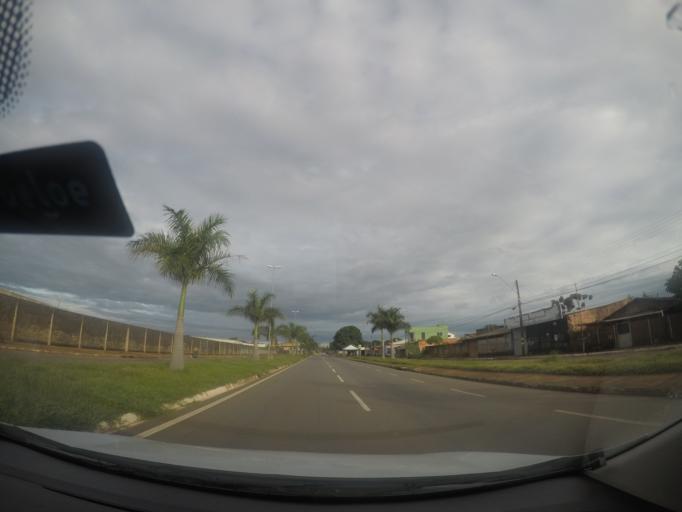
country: BR
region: Goias
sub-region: Goiania
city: Goiania
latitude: -16.6312
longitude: -49.3265
